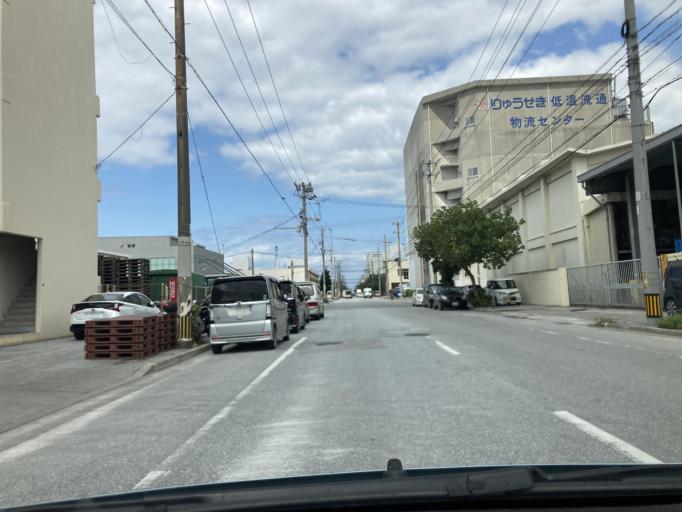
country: JP
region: Okinawa
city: Naha-shi
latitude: 26.2438
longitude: 127.6732
